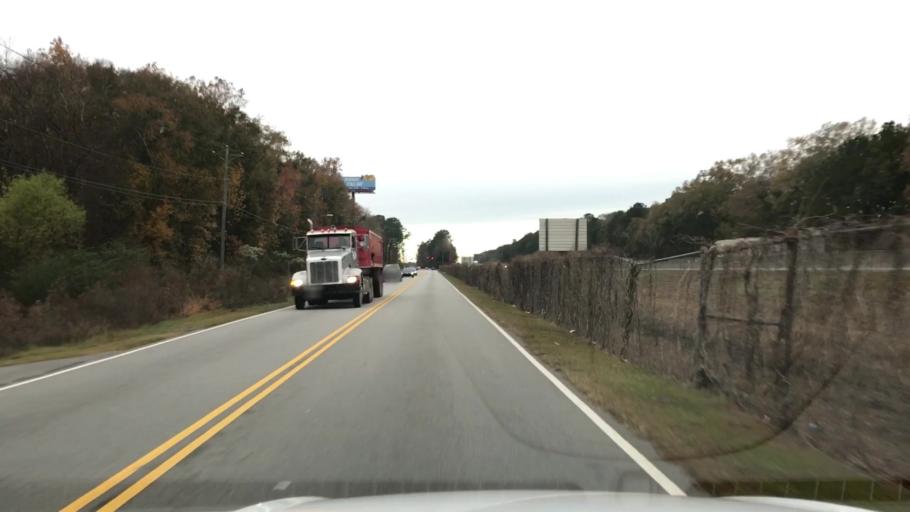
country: US
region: South Carolina
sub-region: Berkeley County
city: Goose Creek
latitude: 32.9462
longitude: -80.0563
